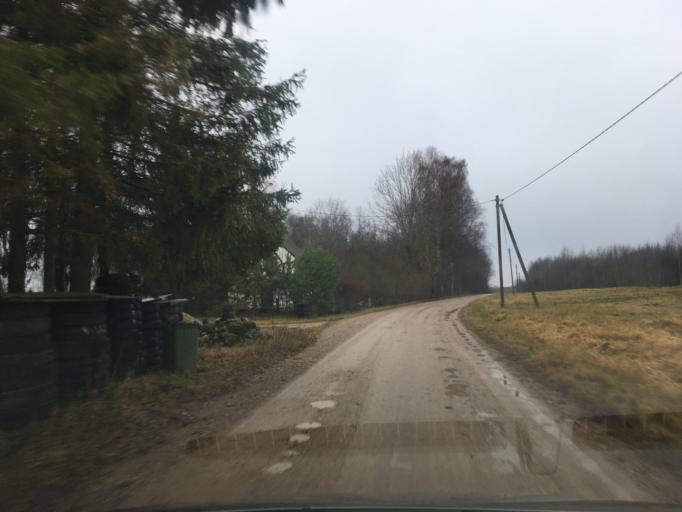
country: EE
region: Tartu
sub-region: Tartu linn
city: Tartu
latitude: 58.3907
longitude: 27.0029
